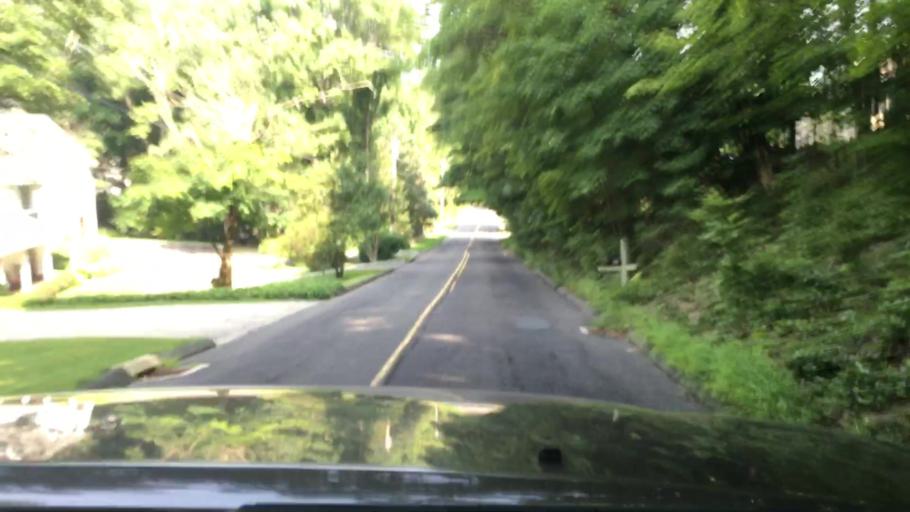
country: US
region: Connecticut
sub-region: Fairfield County
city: Georgetown
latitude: 41.2642
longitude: -73.4545
